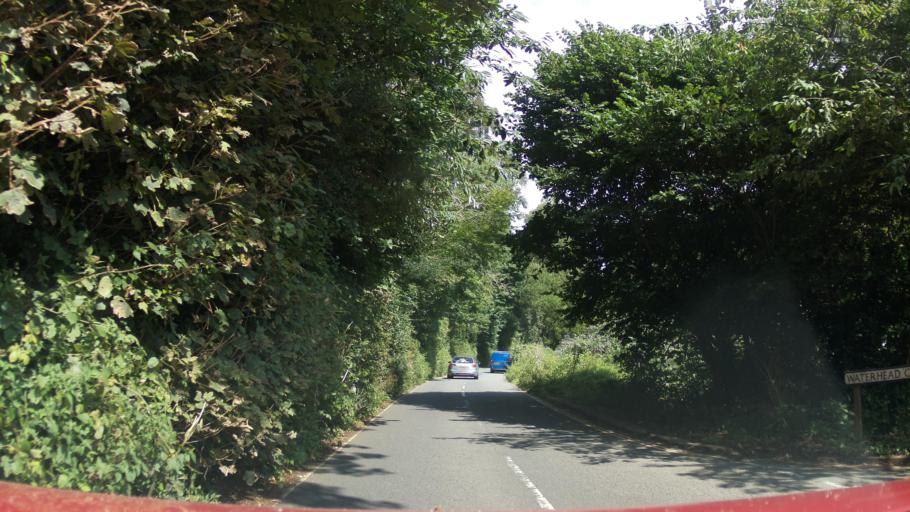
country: GB
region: England
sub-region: Devon
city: Dartmouth
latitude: 50.3549
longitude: -3.5636
